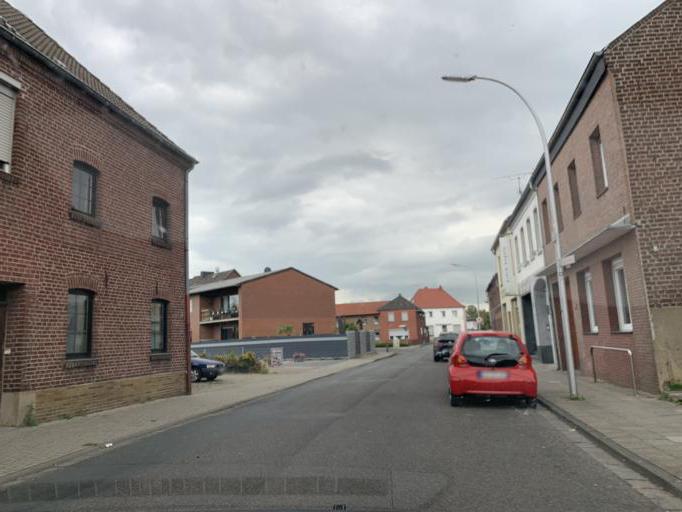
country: DE
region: North Rhine-Westphalia
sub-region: Regierungsbezirk Koln
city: Wassenberg
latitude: 51.0618
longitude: 6.1426
